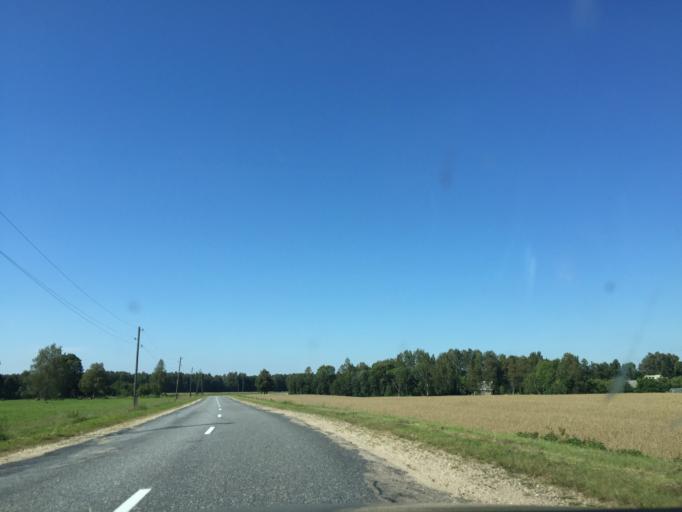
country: LV
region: Limbazu Rajons
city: Limbazi
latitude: 57.4627
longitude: 24.7178
